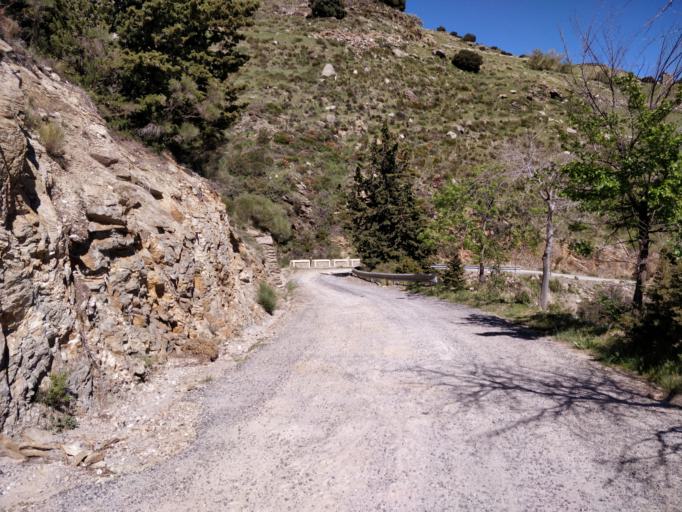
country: ES
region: Andalusia
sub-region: Provincia de Granada
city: Soportujar
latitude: 36.9355
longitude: -3.4027
